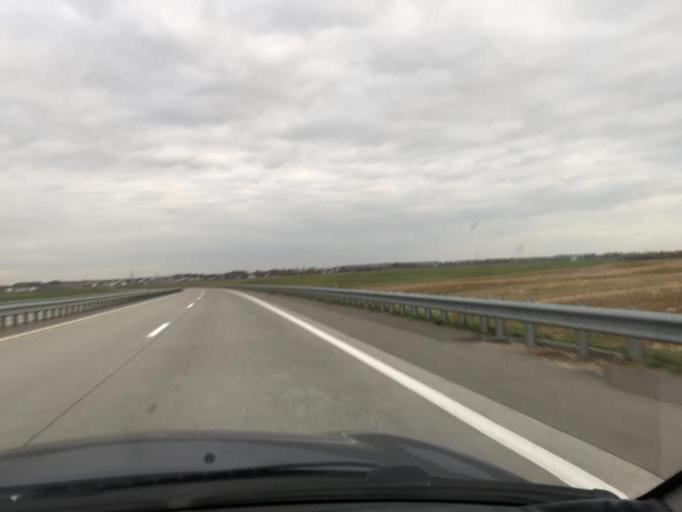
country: BY
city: Fanipol
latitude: 53.7659
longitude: 27.3708
